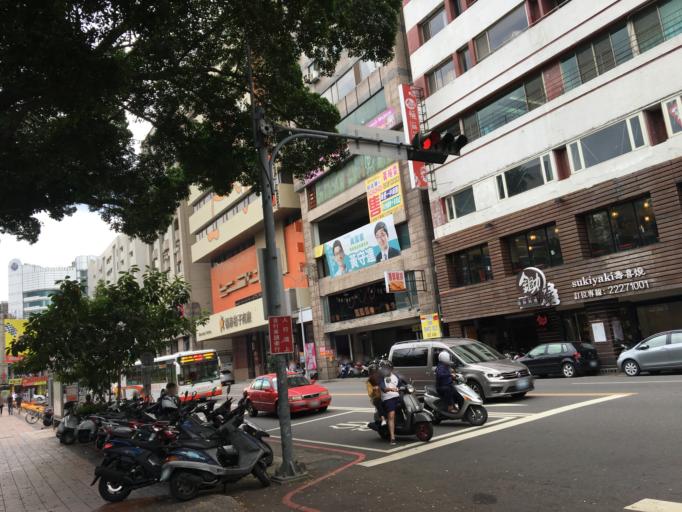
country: TW
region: Taiwan
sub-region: Taichung City
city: Taichung
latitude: 24.1430
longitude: 120.6837
